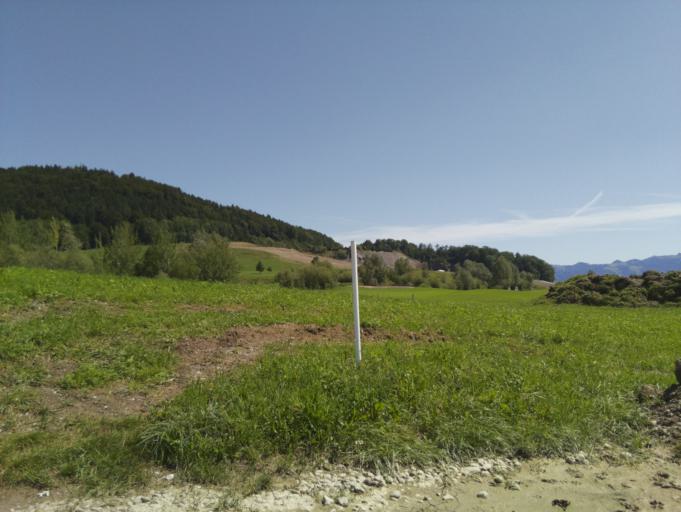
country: CH
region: Schwyz
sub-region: Bezirk March
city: Schubelbach
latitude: 47.1951
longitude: 8.9026
